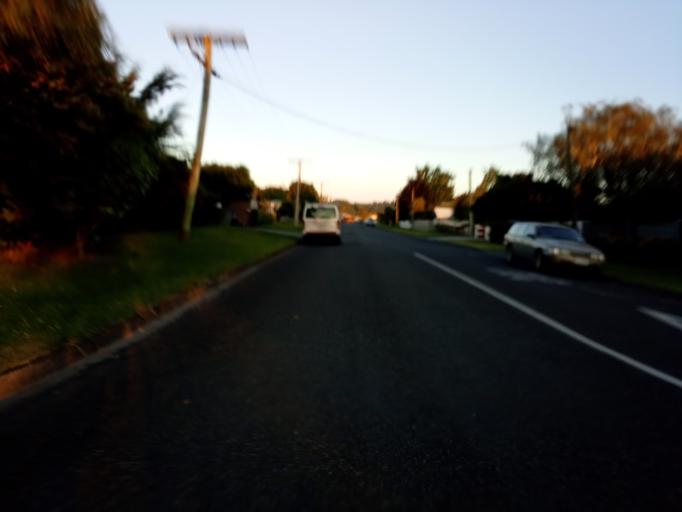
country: NZ
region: Gisborne
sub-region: Gisborne District
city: Gisborne
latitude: -38.6423
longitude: 178.0025
